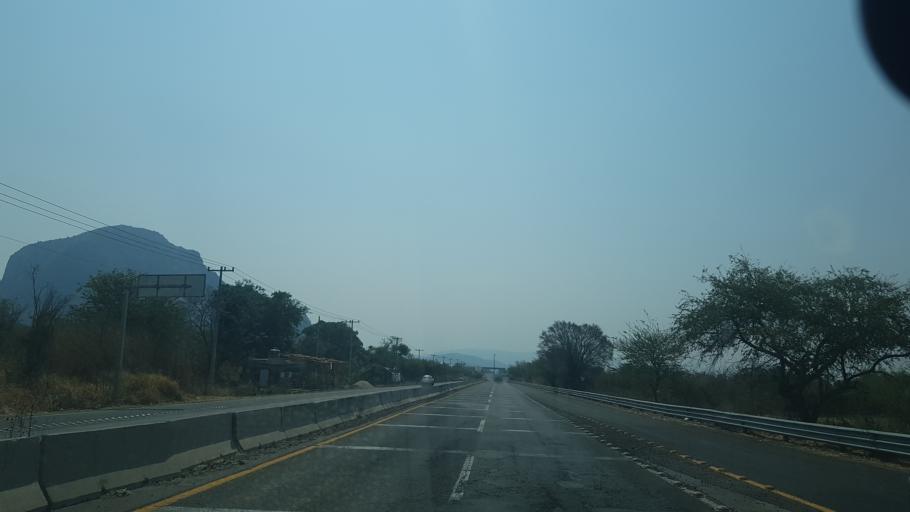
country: MX
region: Morelos
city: Jantetelco
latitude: 18.7083
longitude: -98.7772
